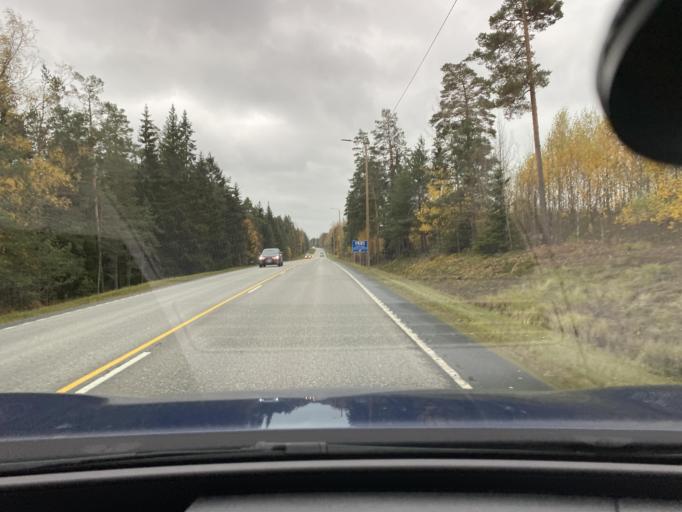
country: FI
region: Varsinais-Suomi
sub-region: Vakka-Suomi
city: Laitila
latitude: 60.9667
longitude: 21.5941
